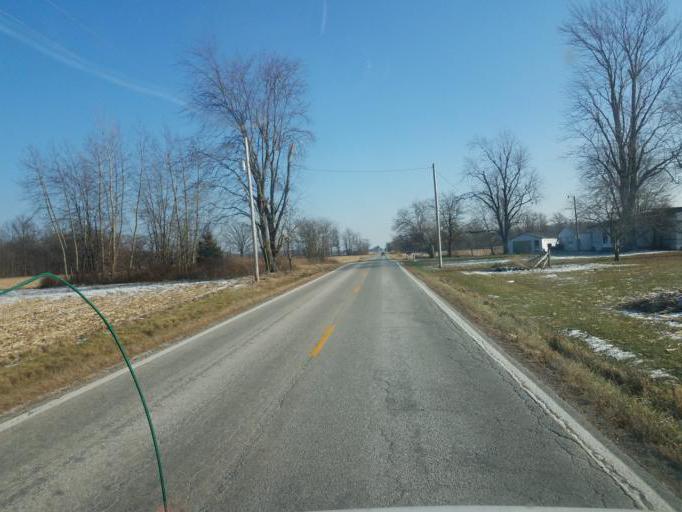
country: US
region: Ohio
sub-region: Morrow County
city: Cardington
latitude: 40.5327
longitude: -82.9849
